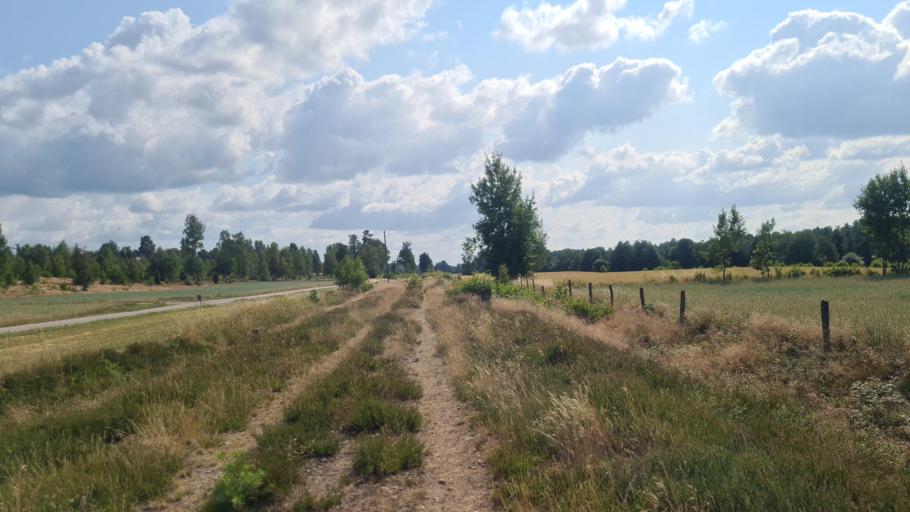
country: SE
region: Kronoberg
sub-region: Ljungby Kommun
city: Ljungby
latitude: 56.7510
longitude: 13.8831
